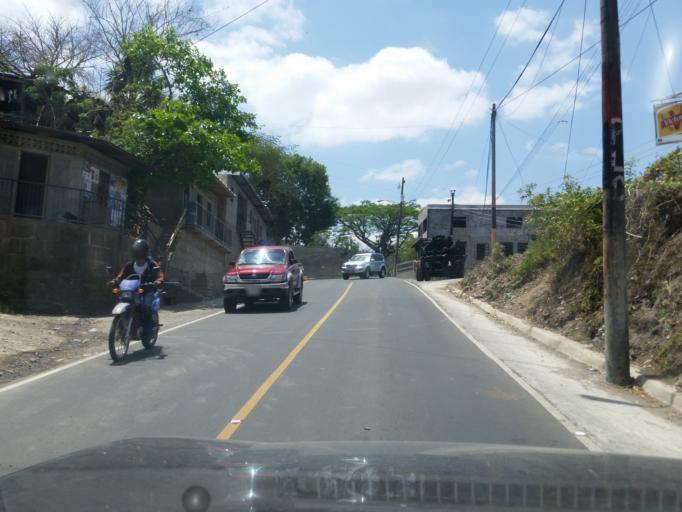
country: NI
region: Boaco
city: Boaco
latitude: 12.4700
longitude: -85.6519
